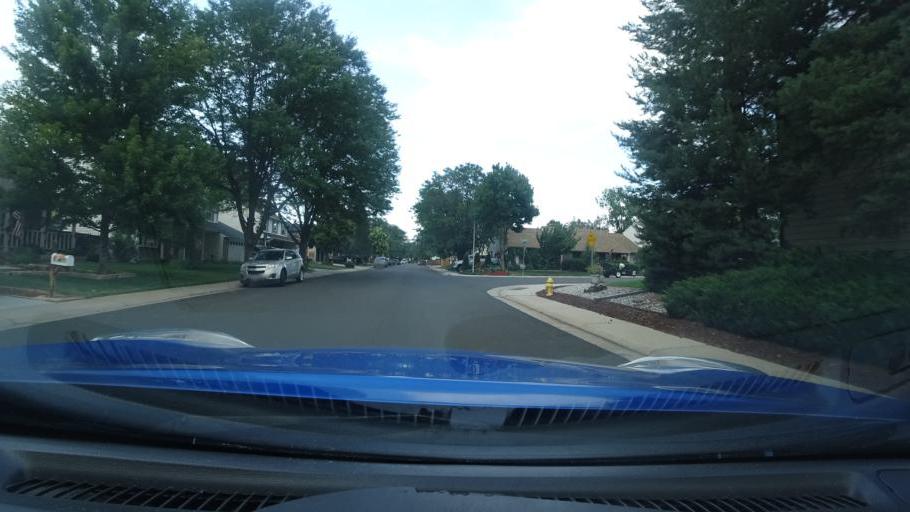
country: US
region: Colorado
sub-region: Adams County
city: Aurora
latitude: 39.6930
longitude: -104.8017
